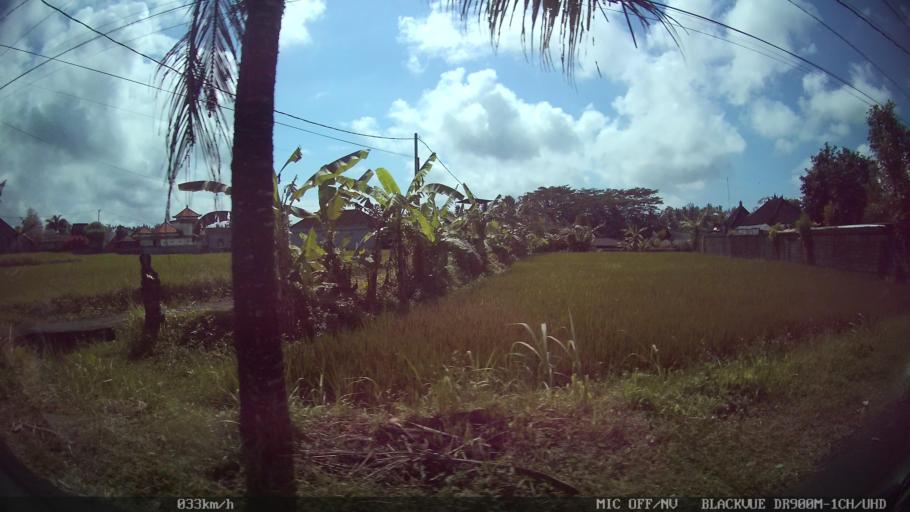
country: ID
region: Bali
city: Banjar Tebongkang
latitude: -8.5529
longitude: 115.2751
